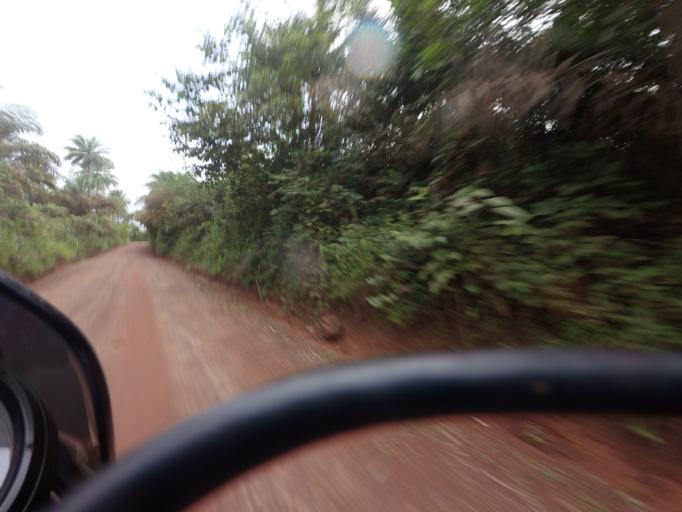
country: SL
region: Northern Province
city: Kambia
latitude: 9.1593
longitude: -12.8788
